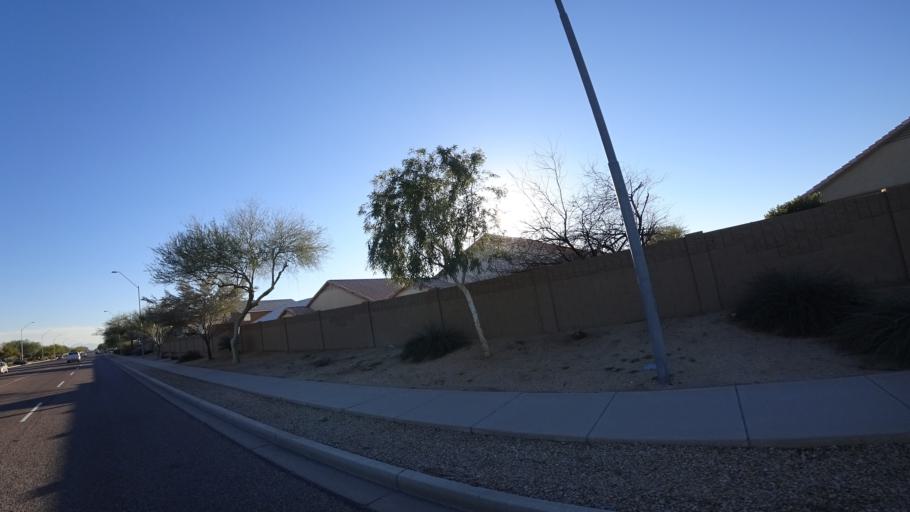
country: US
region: Arizona
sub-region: Maricopa County
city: Sun City West
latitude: 33.6801
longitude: -112.2899
